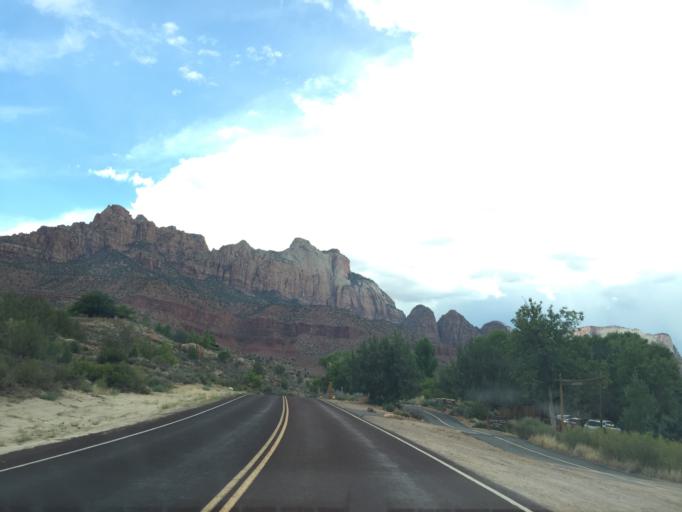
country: US
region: Utah
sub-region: Washington County
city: Hildale
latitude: 37.1699
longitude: -113.0132
